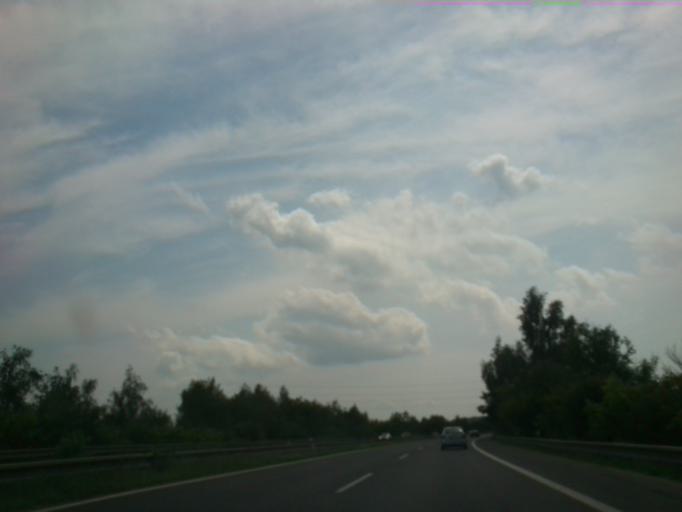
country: CZ
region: Central Bohemia
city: Brandys nad Labem-Stara Boleslav
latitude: 50.1852
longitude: 14.6959
